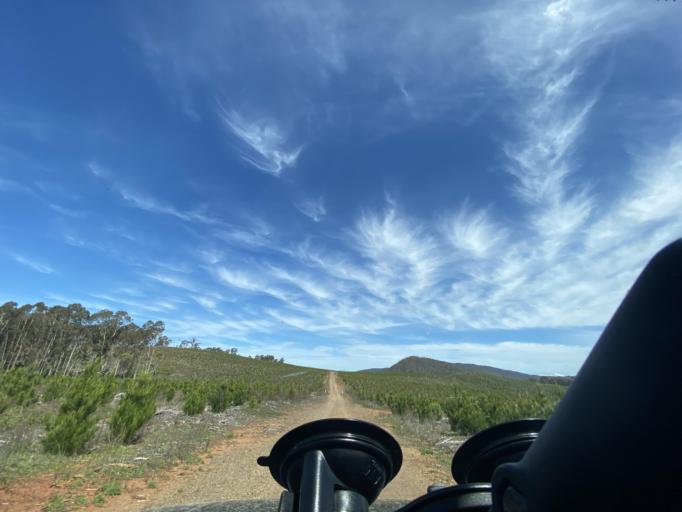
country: AU
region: Victoria
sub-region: Mansfield
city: Mansfield
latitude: -36.8193
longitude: 146.1023
